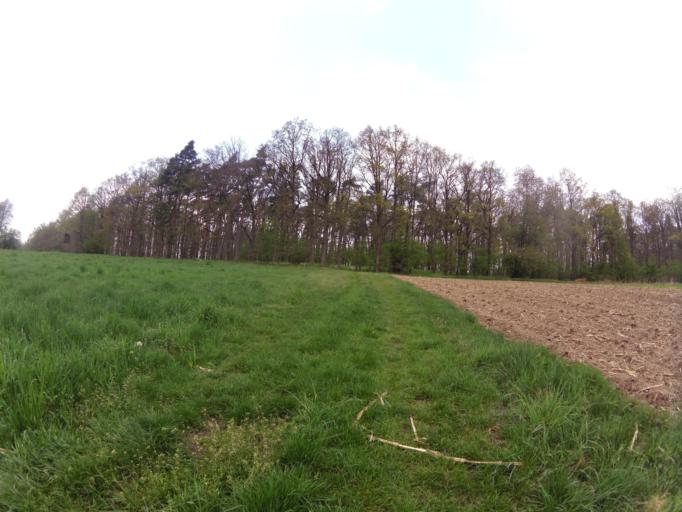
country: DE
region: Bavaria
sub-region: Regierungsbezirk Unterfranken
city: Ochsenfurt
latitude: 49.6994
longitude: 10.0633
